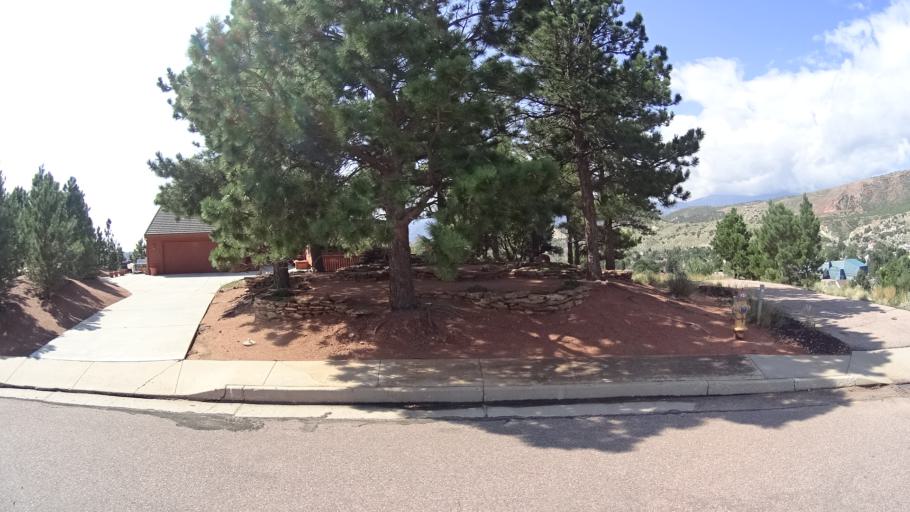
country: US
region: Colorado
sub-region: El Paso County
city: Manitou Springs
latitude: 38.9079
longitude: -104.8683
